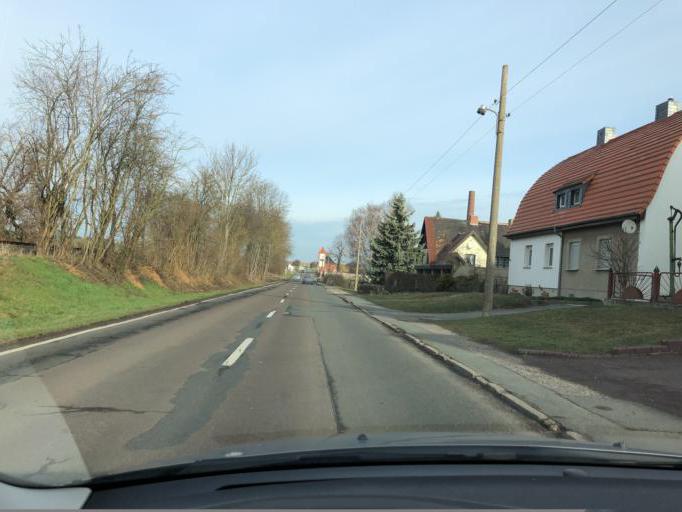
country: DE
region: Saxony-Anhalt
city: Laucha
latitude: 51.2285
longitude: 11.6699
